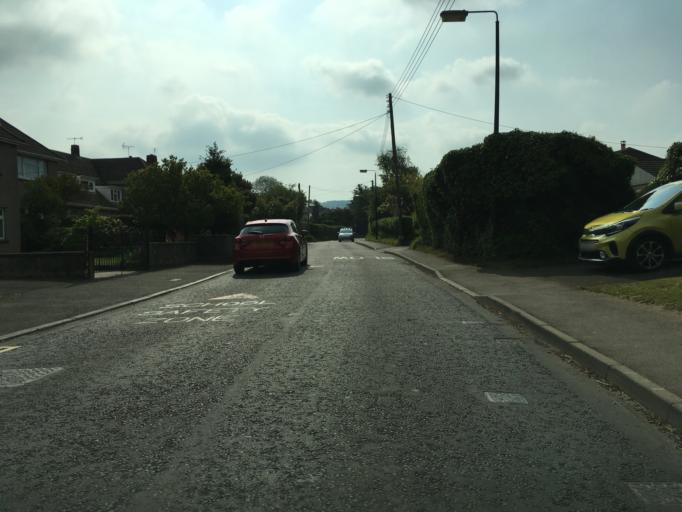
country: GB
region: England
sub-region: North Somerset
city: Nailsea
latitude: 51.4186
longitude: -2.7480
